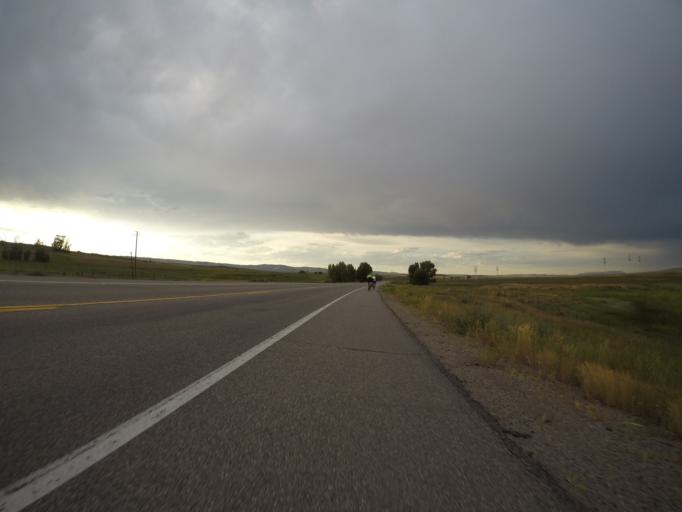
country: US
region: Idaho
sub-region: Bear Lake County
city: Montpelier
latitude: 42.0655
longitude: -110.9376
